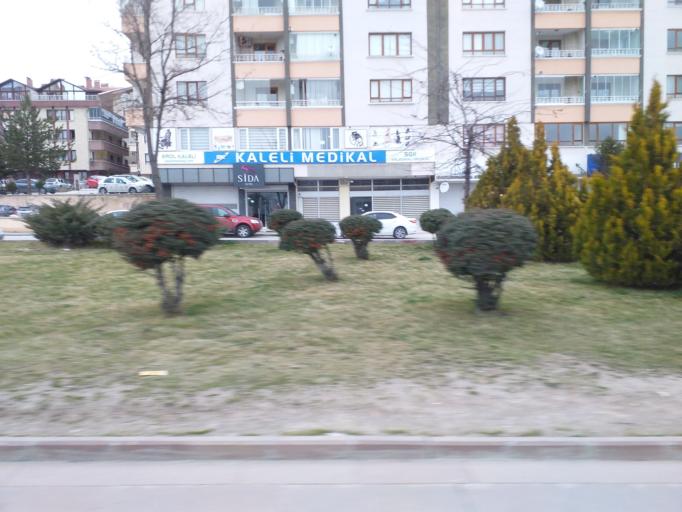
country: TR
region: Ankara
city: Ankara
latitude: 39.9691
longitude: 32.8302
